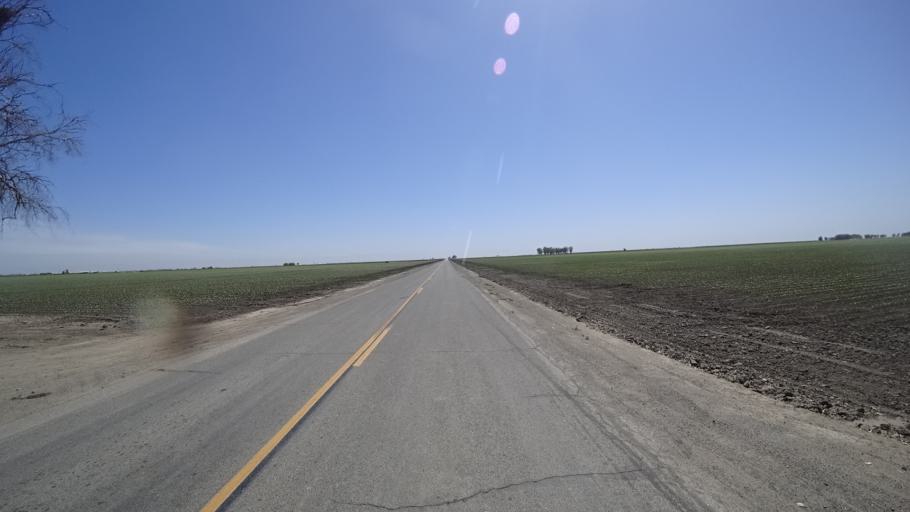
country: US
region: California
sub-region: Kings County
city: Stratford
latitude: 36.1894
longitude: -119.7802
